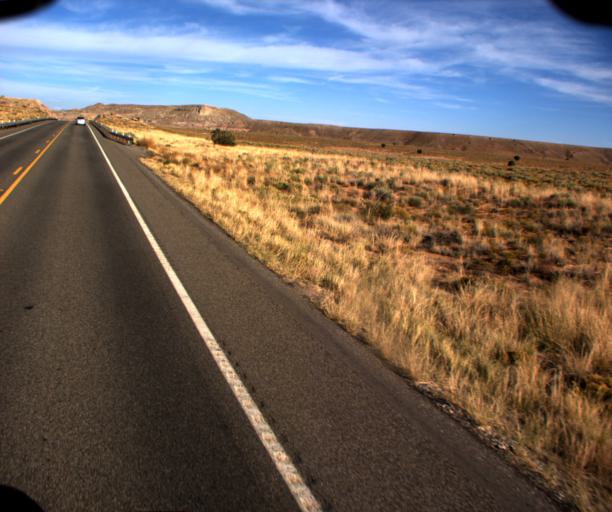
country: US
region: New Mexico
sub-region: San Juan County
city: Shiprock
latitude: 36.9337
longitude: -109.1357
